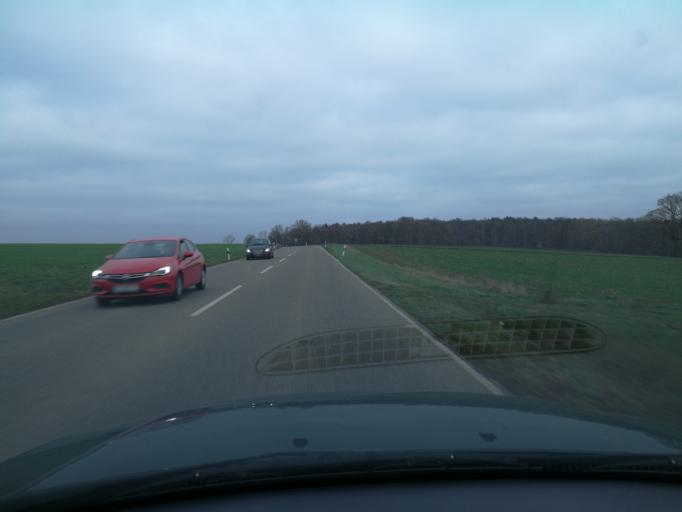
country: DE
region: Bavaria
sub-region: Regierungsbezirk Mittelfranken
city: Seukendorf
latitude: 49.4858
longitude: 10.8944
